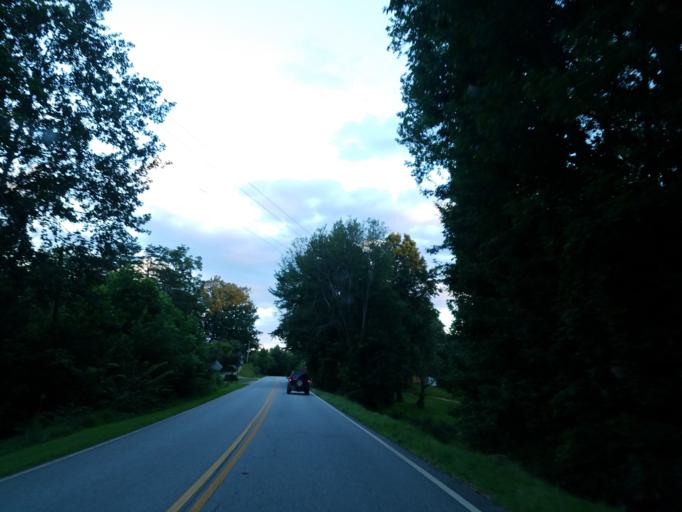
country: US
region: Georgia
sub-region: Lumpkin County
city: Dahlonega
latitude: 34.5959
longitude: -83.9706
